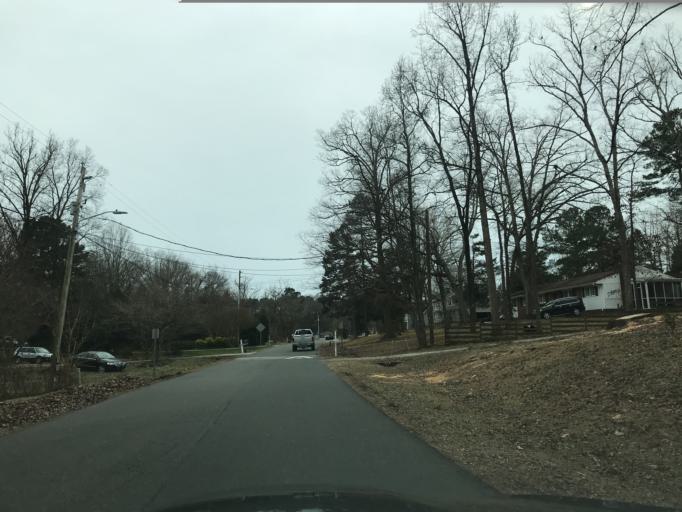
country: US
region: North Carolina
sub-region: Wake County
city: West Raleigh
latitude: 35.8678
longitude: -78.5999
